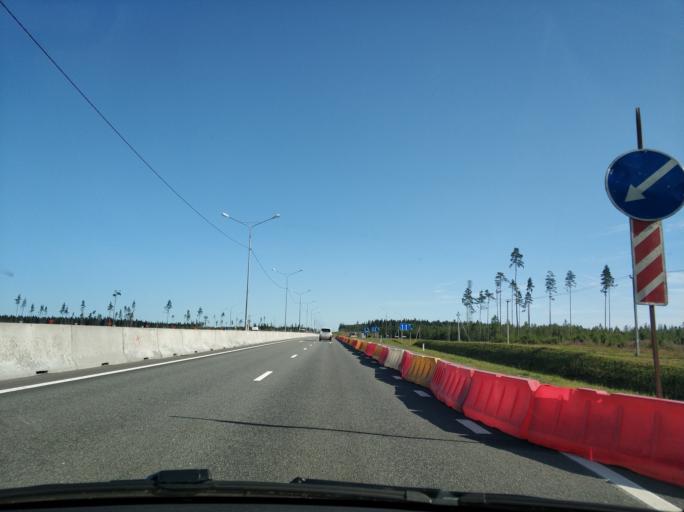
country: RU
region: Leningrad
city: Sosnovo
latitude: 60.4731
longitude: 30.1960
